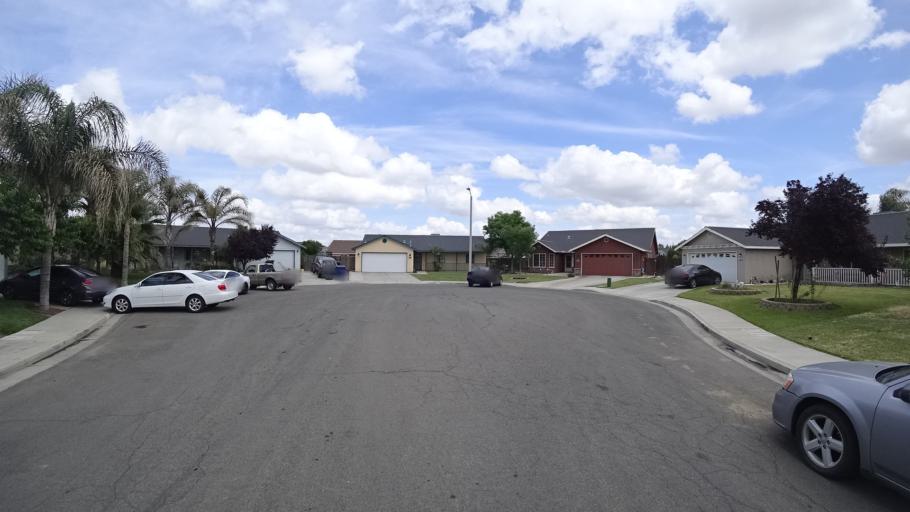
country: US
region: California
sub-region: Kings County
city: Home Garden
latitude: 36.3007
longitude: -119.6574
